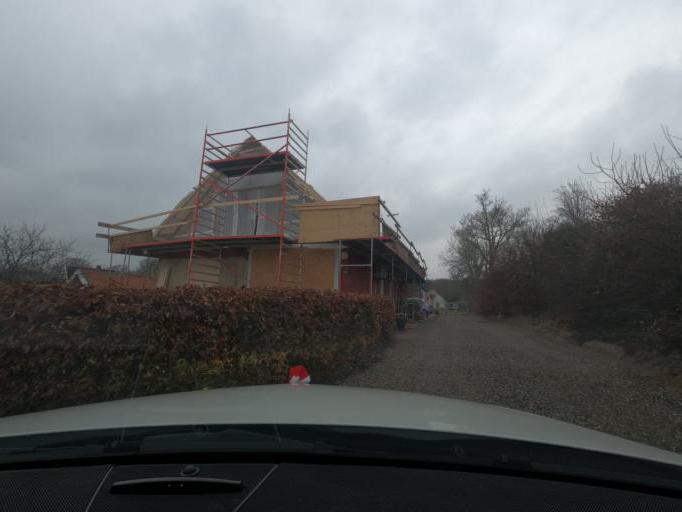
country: DK
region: South Denmark
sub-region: Haderslev Kommune
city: Starup
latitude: 55.1926
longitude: 9.5844
